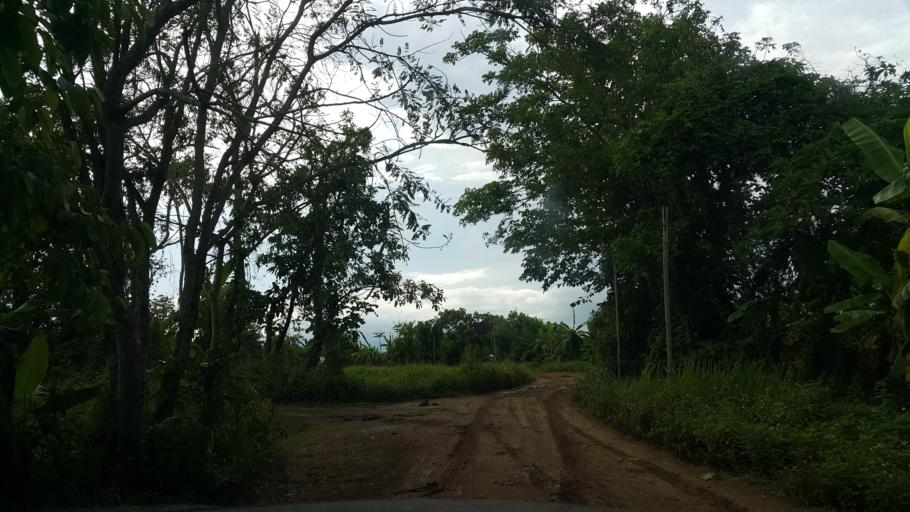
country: TH
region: Chiang Rai
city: Wiang Chai
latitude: 19.9749
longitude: 99.9125
